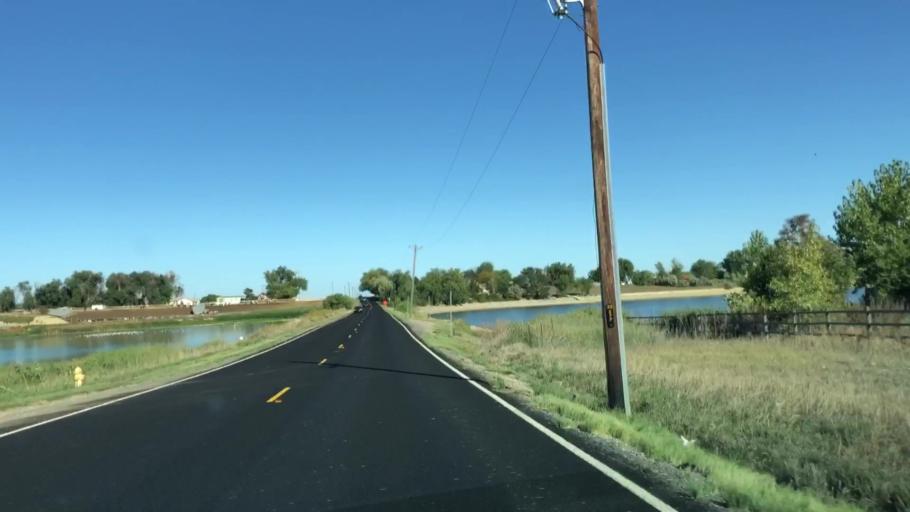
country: US
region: Colorado
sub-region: Larimer County
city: Loveland
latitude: 40.4510
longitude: -105.0544
